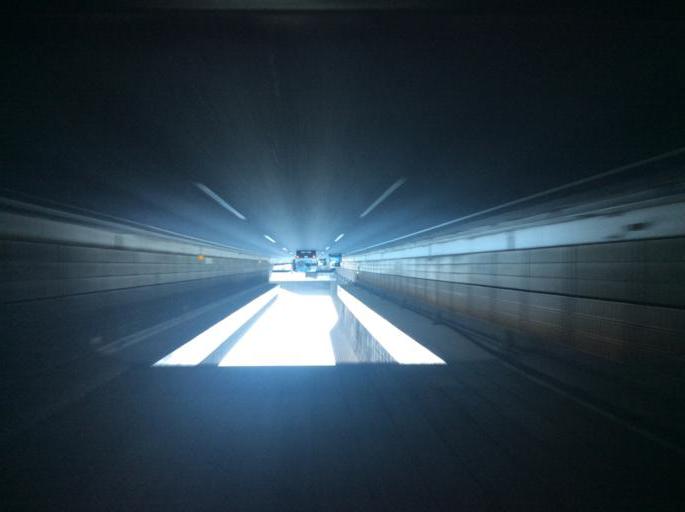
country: JP
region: Chiba
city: Nagareyama
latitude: 35.8893
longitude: 139.9140
